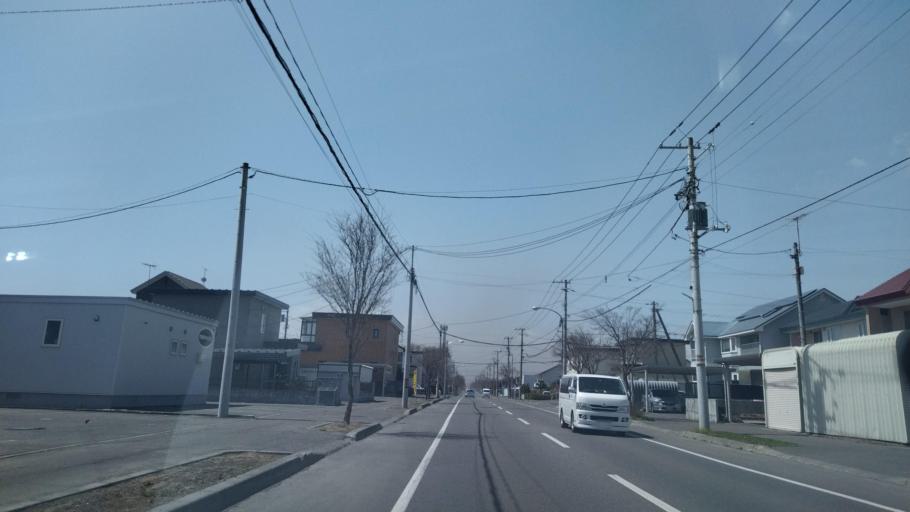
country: JP
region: Hokkaido
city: Obihiro
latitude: 42.9399
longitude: 143.1742
